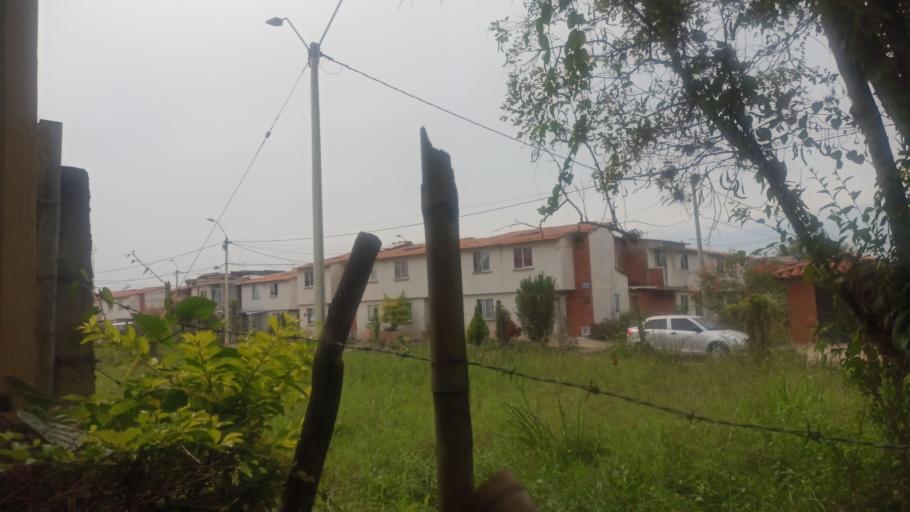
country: CO
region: Valle del Cauca
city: Jamundi
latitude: 3.2331
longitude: -76.5114
